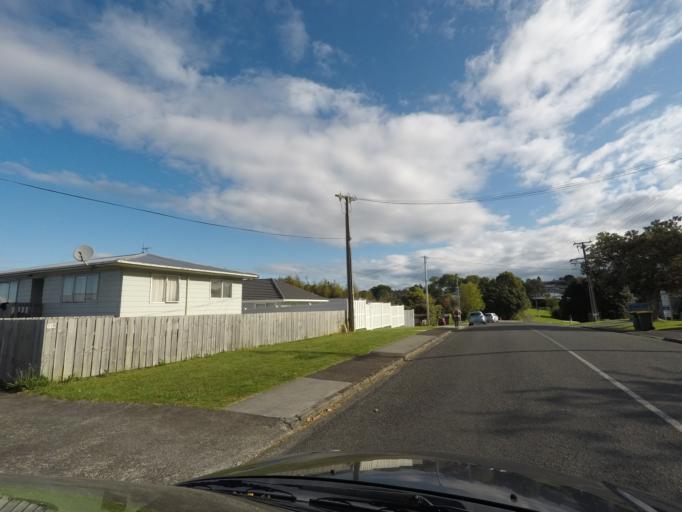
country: NZ
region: Auckland
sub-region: Auckland
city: Rosebank
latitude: -36.8811
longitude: 174.6531
